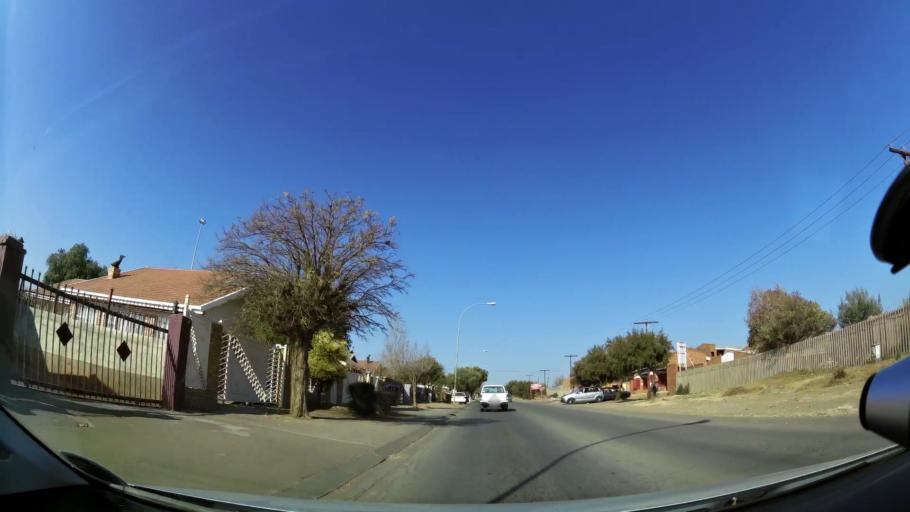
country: ZA
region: Orange Free State
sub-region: Mangaung Metropolitan Municipality
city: Bloemfontein
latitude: -29.1873
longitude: 26.2221
